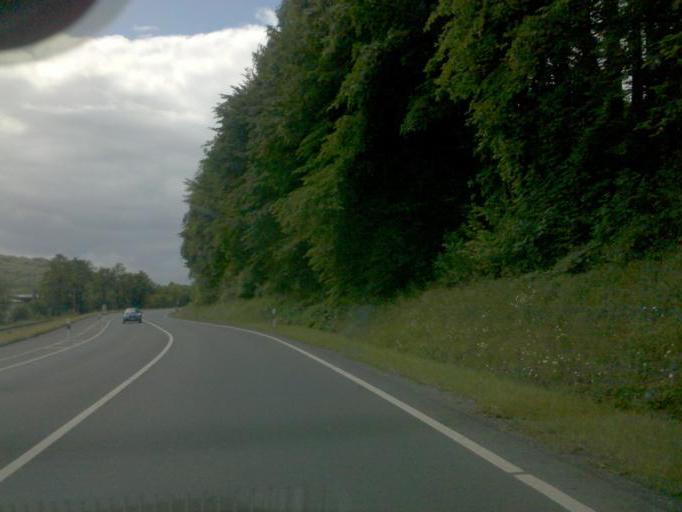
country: DE
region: North Rhine-Westphalia
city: Warstein
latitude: 51.4717
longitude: 8.3393
